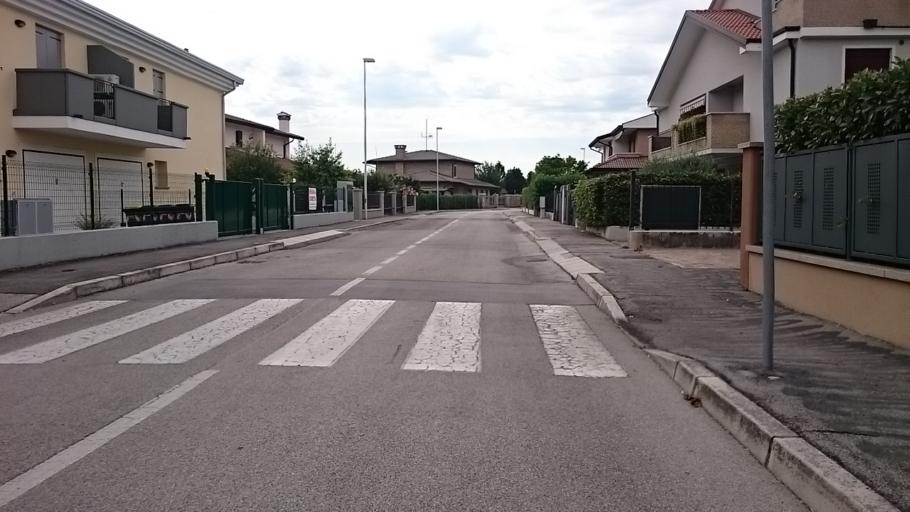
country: IT
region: Veneto
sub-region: Provincia di Padova
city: Albignasego
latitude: 45.3610
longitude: 11.8884
